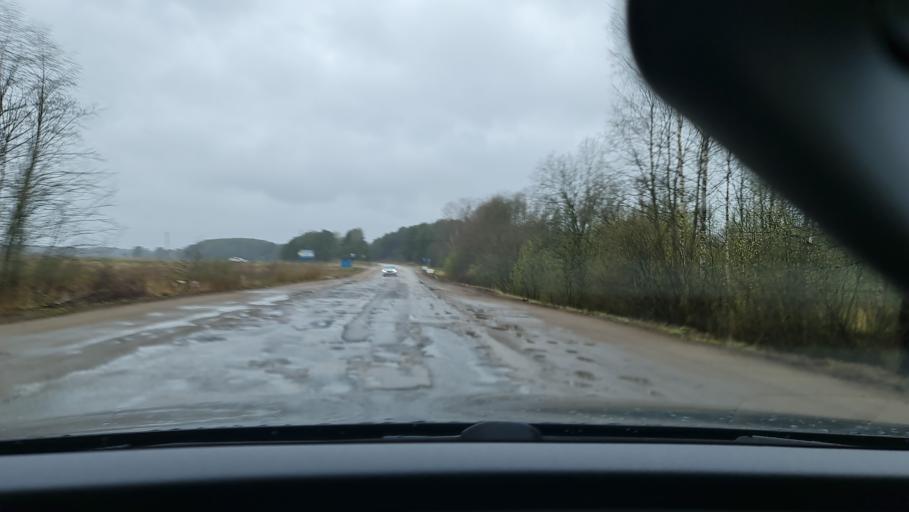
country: RU
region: Novgorod
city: Valday
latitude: 58.0391
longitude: 32.9312
